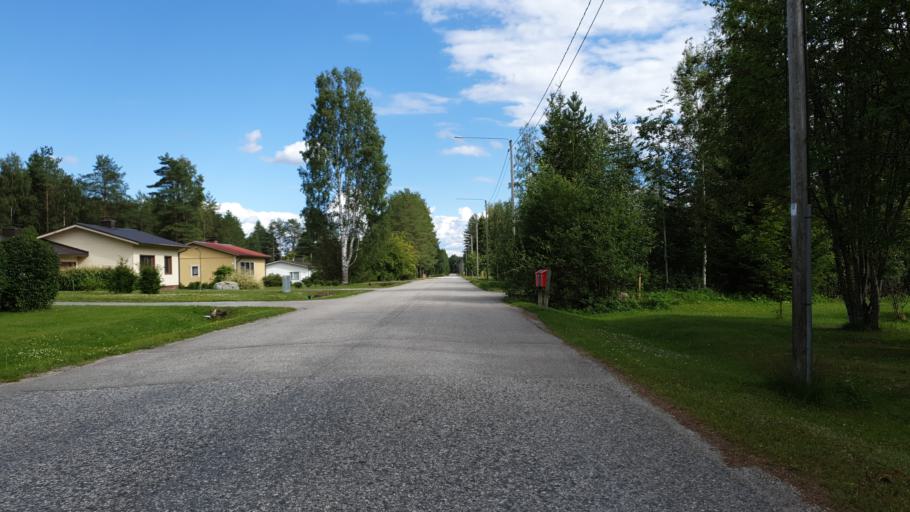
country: FI
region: Kainuu
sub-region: Kehys-Kainuu
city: Kuhmo
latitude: 64.1202
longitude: 29.5503
